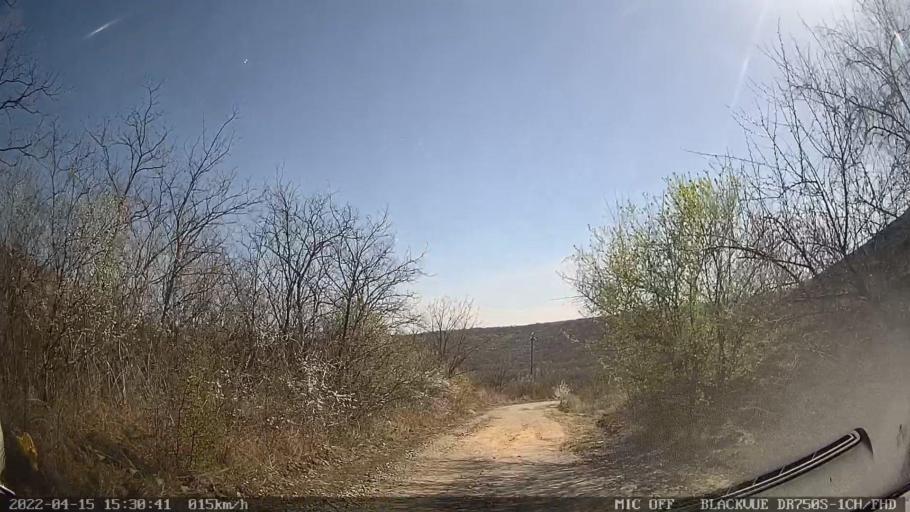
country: MD
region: Raionul Ocnita
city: Otaci
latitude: 48.3542
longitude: 27.9227
